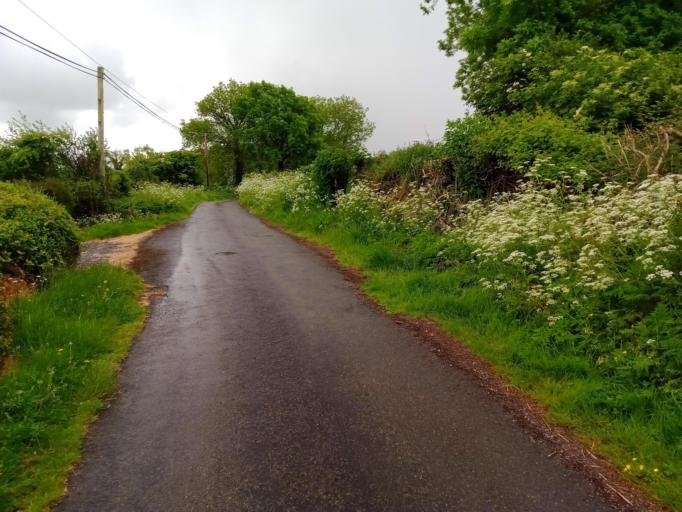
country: IE
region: Leinster
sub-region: Kilkenny
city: Thomastown
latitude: 52.5155
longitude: -7.1351
